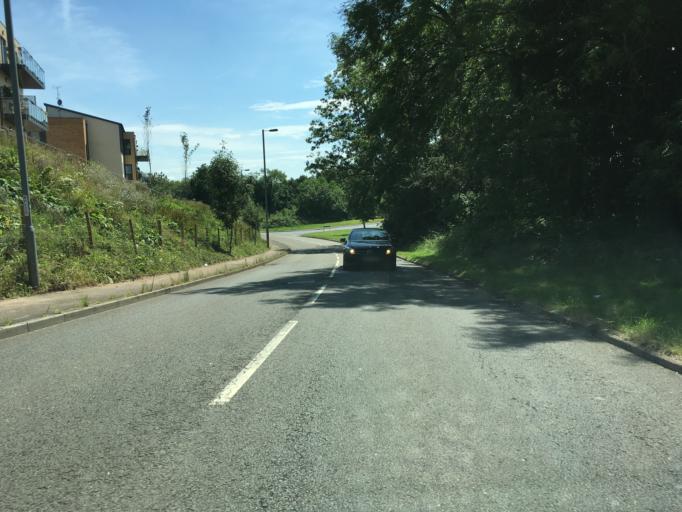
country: GB
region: Wales
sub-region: Newport
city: Newport
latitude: 51.5743
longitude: -3.0180
